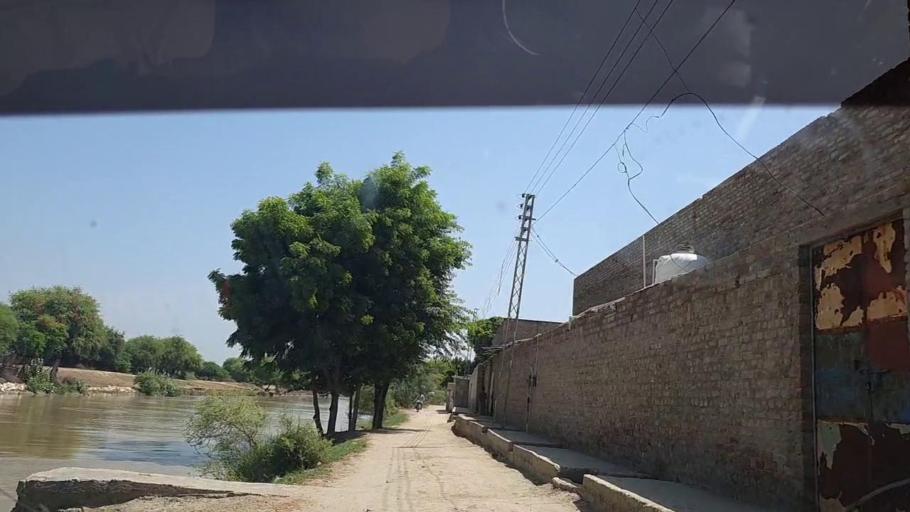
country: PK
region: Sindh
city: Ghauspur
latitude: 28.1661
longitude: 69.1275
